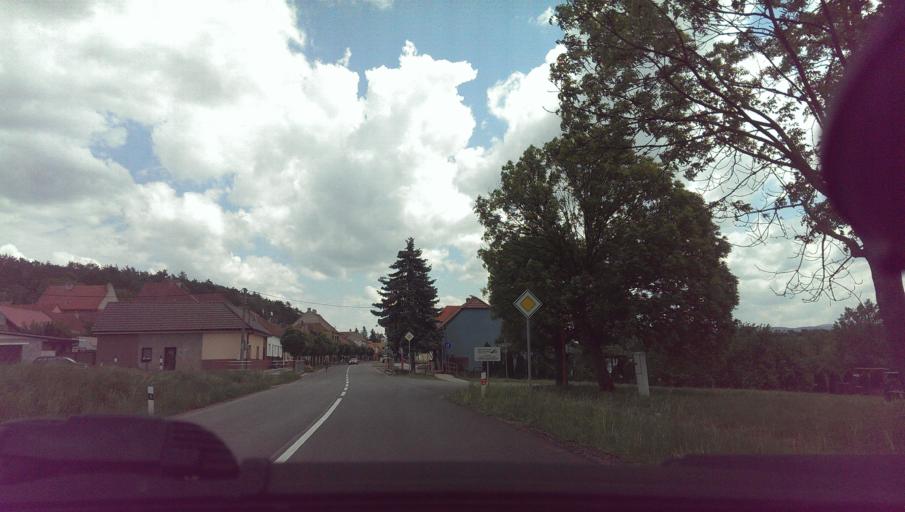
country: CZ
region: Zlin
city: Dolni Nemci
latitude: 48.9702
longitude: 17.5728
